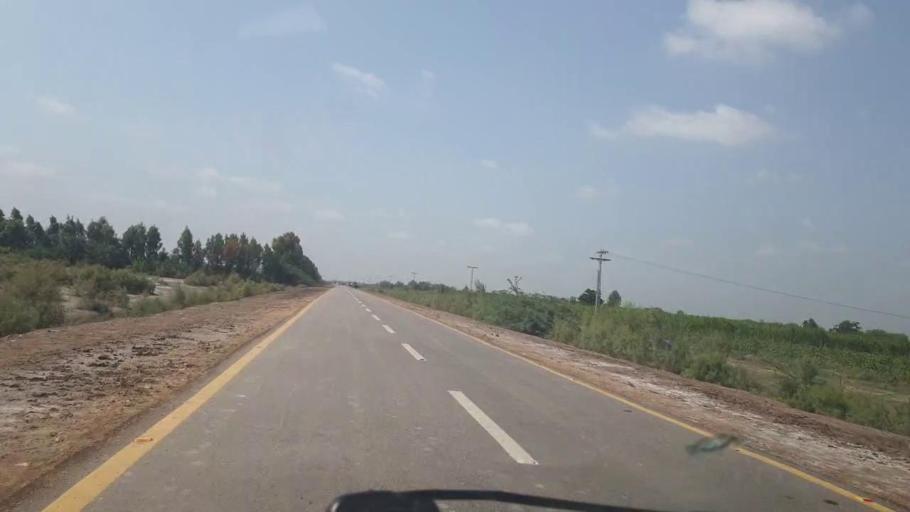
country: PK
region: Sindh
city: Berani
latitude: 25.7357
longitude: 68.9442
